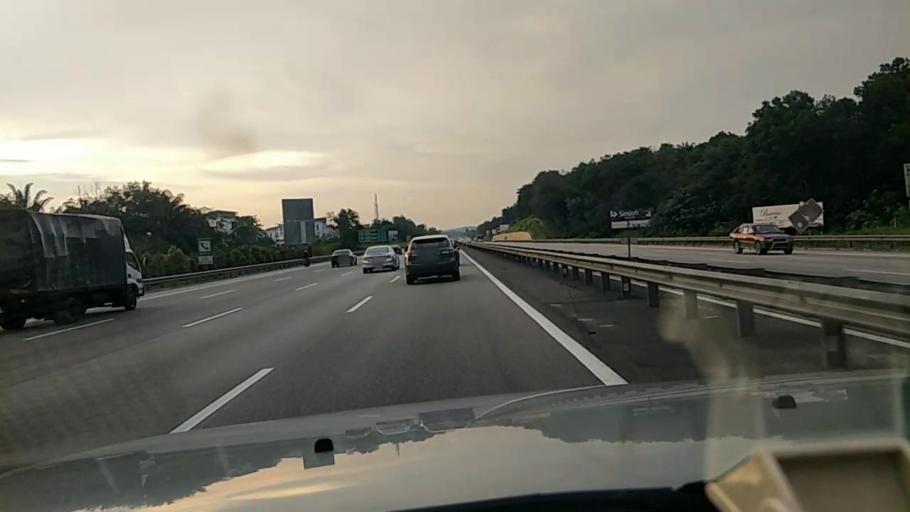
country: MY
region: Selangor
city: Kuang
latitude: 3.2508
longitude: 101.5633
